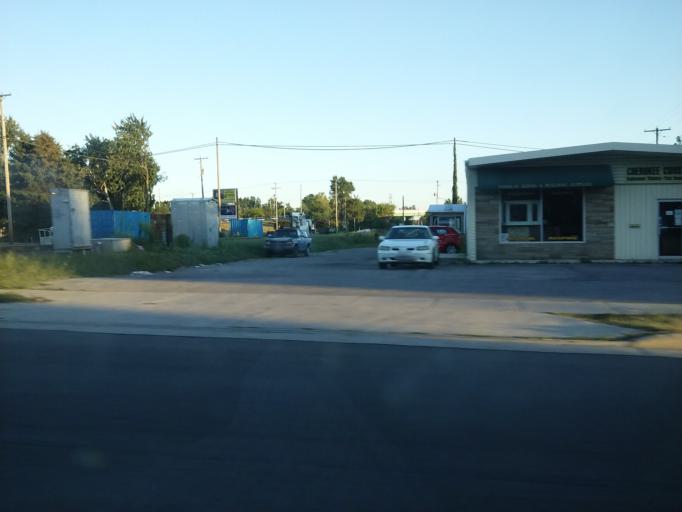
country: US
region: Ohio
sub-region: Hancock County
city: Findlay
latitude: 41.0441
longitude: -83.6445
